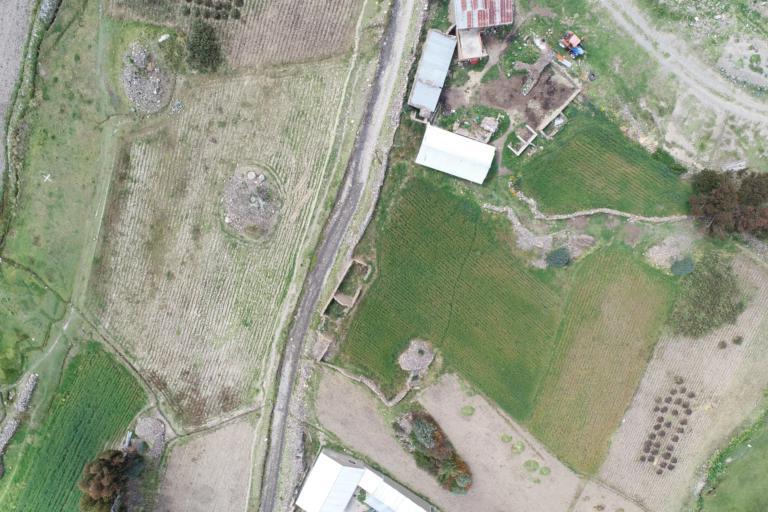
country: BO
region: La Paz
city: Achacachi
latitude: -16.0209
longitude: -68.6213
